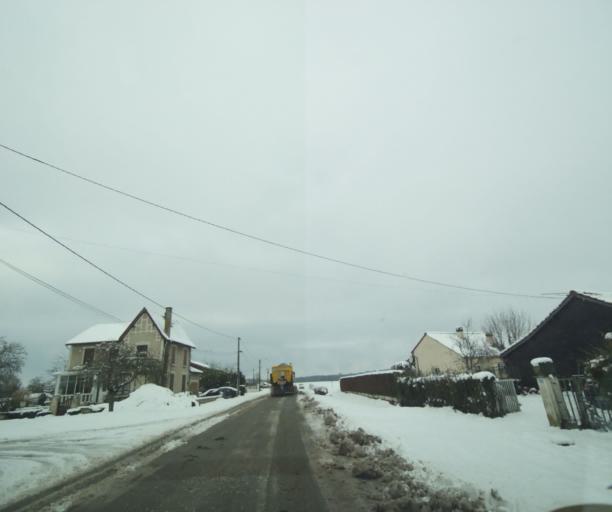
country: FR
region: Champagne-Ardenne
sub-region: Departement de la Haute-Marne
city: Montier-en-Der
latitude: 48.4905
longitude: 4.6982
